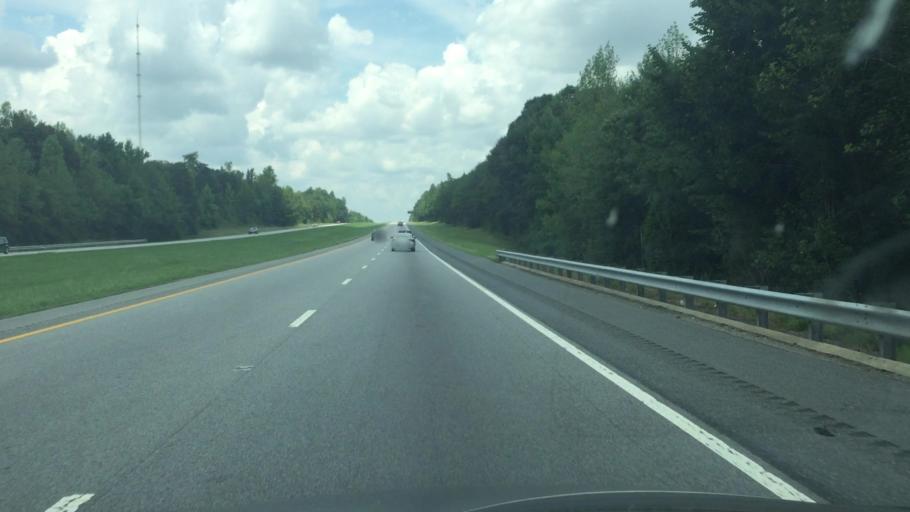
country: US
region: North Carolina
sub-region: Guilford County
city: Pleasant Garden
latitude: 35.9577
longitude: -79.8200
